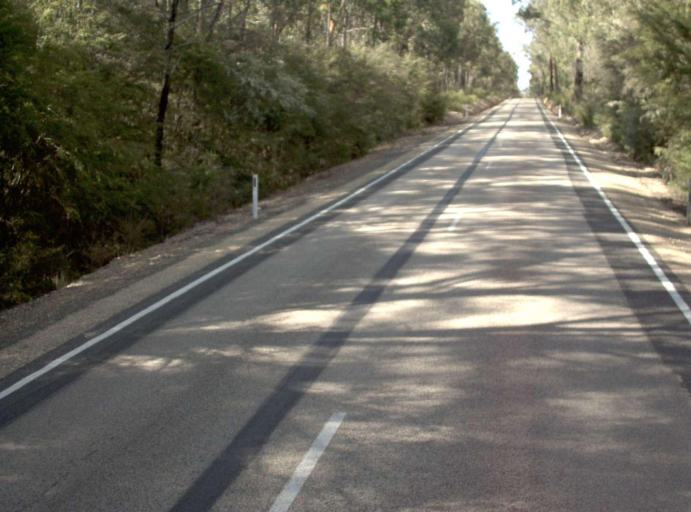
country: AU
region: Victoria
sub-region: East Gippsland
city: Lakes Entrance
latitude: -37.6754
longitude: 148.0555
